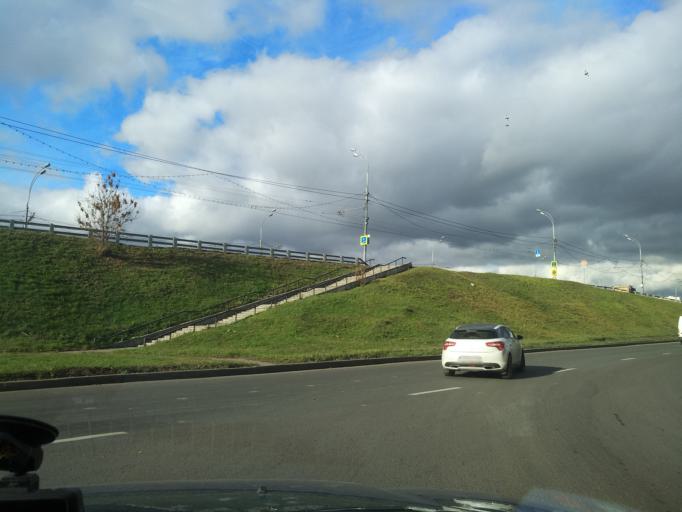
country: RU
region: Moscow
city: Slobodka
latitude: 55.8702
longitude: 37.5862
